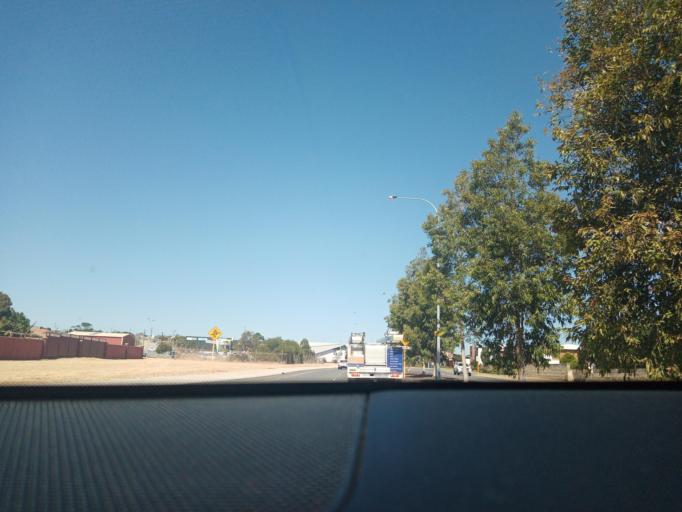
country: AU
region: Western Australia
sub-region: City of Cockburn
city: Beeliar
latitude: -32.1269
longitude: 115.7945
